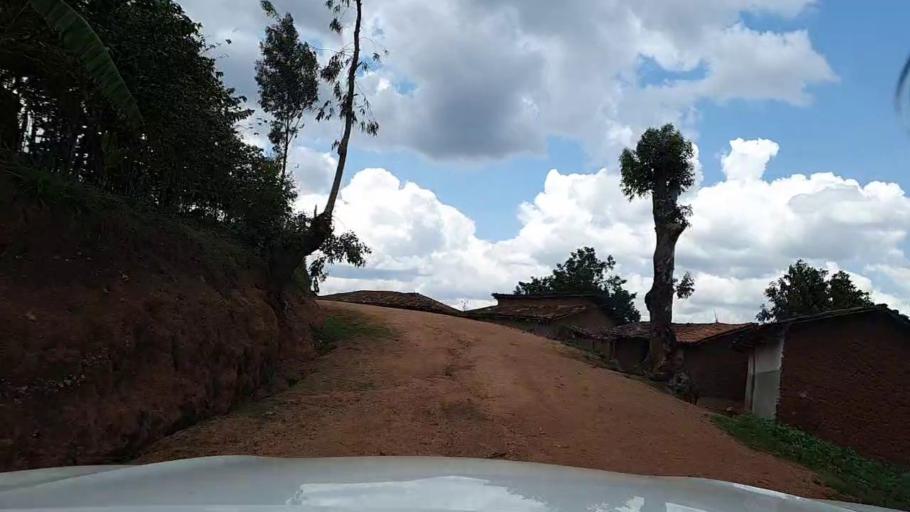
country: RW
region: Southern Province
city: Butare
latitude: -2.7519
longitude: 29.7592
